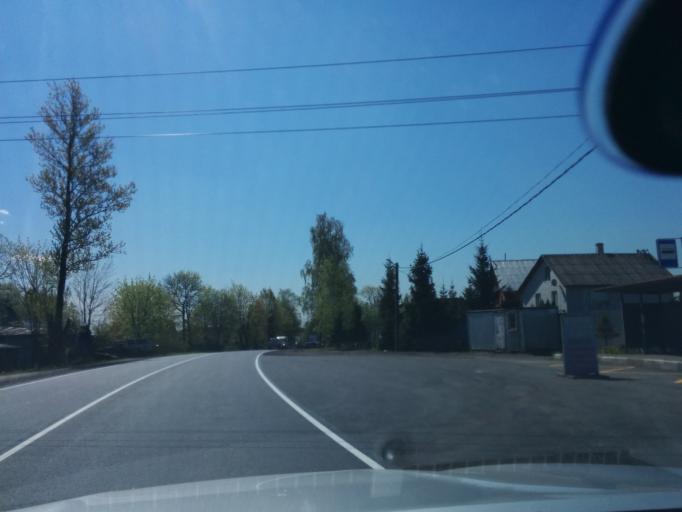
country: RU
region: Leningrad
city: Verkhniye Osel'ki
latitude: 60.2216
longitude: 30.4341
